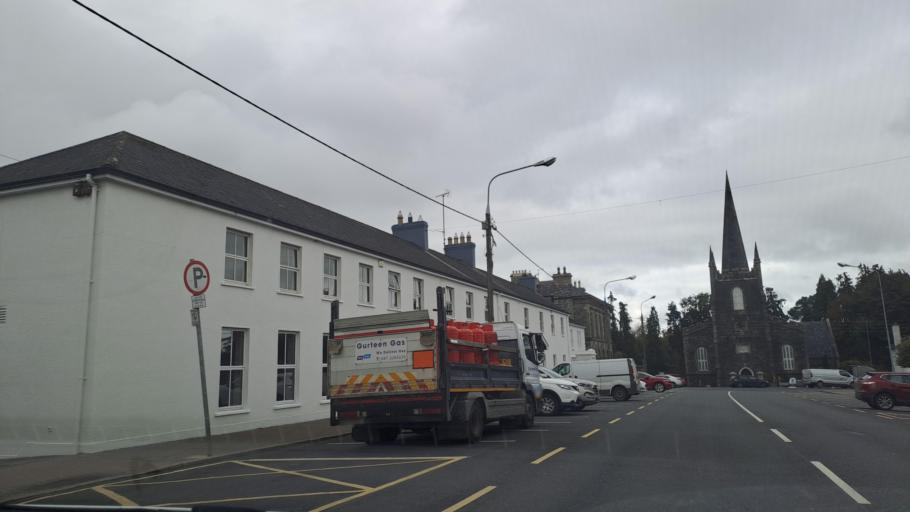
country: IE
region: Ulster
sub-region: An Cabhan
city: Cootehill
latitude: 54.0745
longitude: -7.0802
